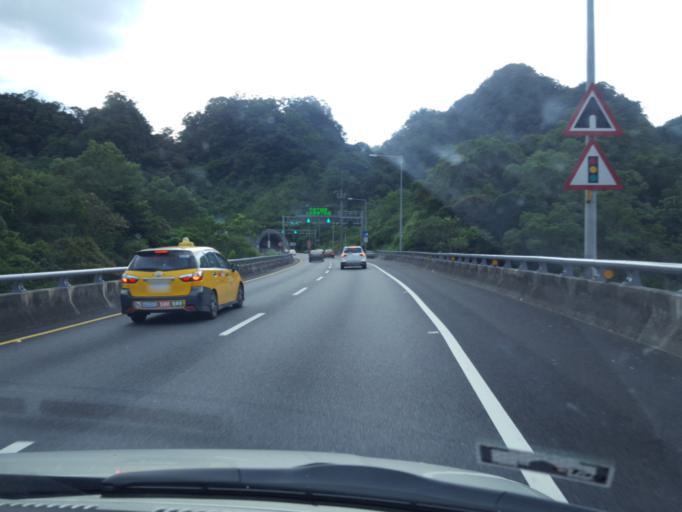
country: TW
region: Taipei
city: Taipei
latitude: 24.9823
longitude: 121.6697
